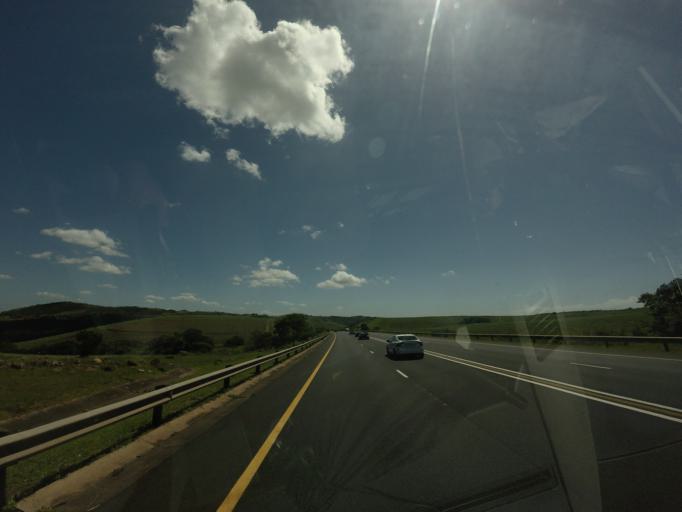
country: ZA
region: KwaZulu-Natal
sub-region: iLembe District Municipality
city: Mandeni
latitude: -29.1004
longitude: 31.5866
